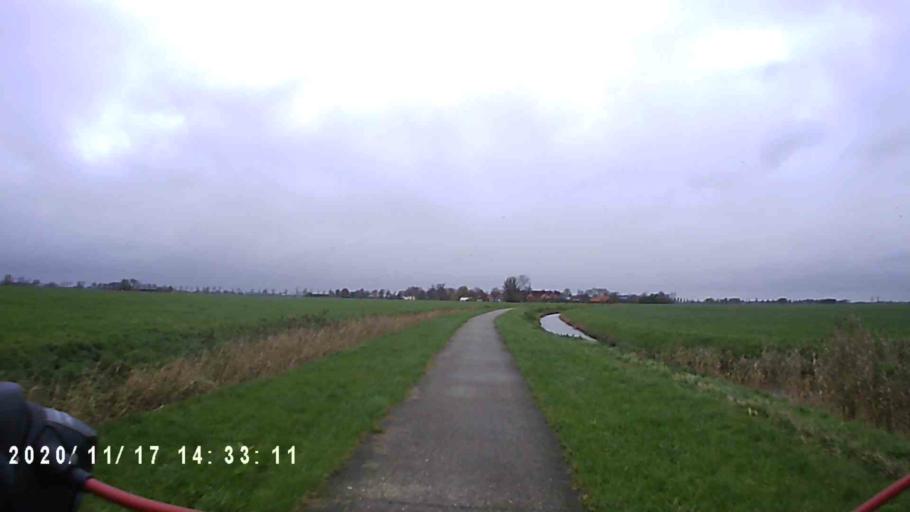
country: NL
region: Groningen
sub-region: Gemeente Zuidhorn
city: Oldehove
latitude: 53.2849
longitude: 6.3626
